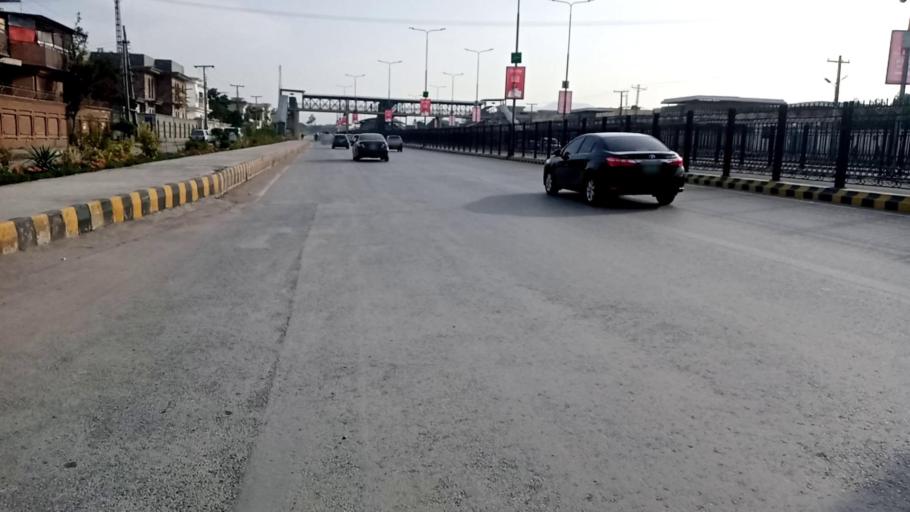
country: PK
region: Khyber Pakhtunkhwa
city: Peshawar
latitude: 33.9878
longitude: 71.4432
